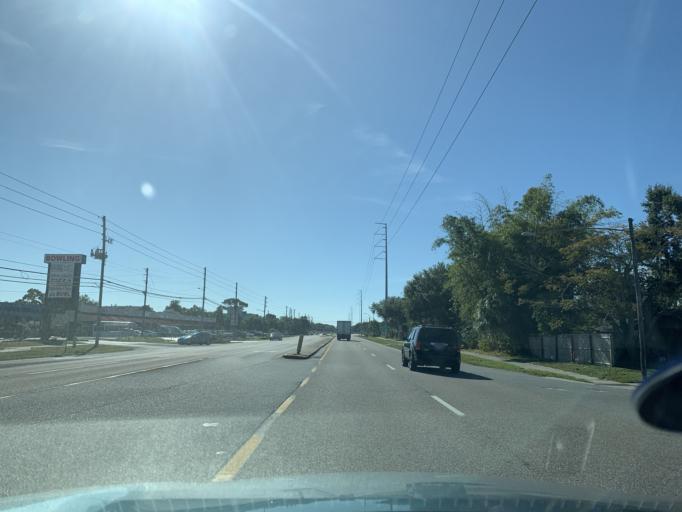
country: US
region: Florida
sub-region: Pinellas County
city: Largo
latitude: 27.8774
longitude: -82.7624
